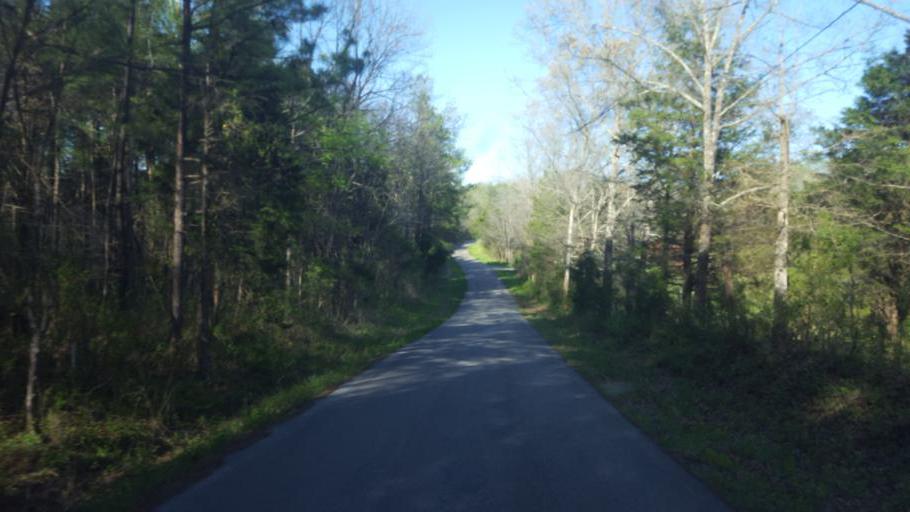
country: US
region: Kentucky
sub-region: Barren County
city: Cave City
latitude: 37.1976
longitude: -86.0381
